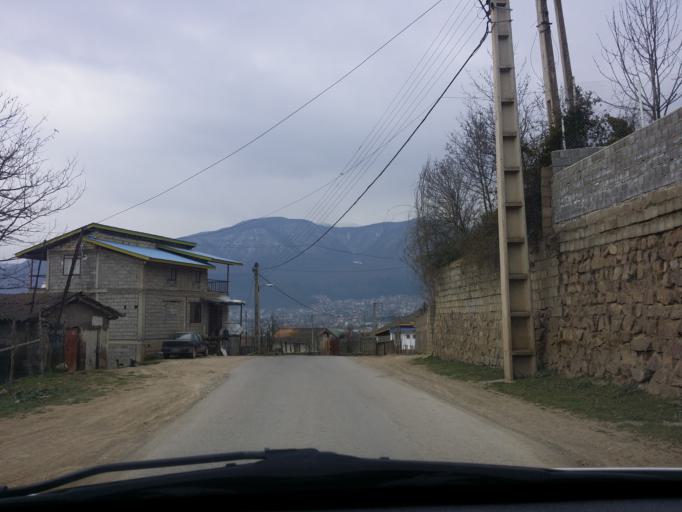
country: IR
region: Mazandaran
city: `Abbasabad
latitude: 36.5307
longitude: 51.1603
